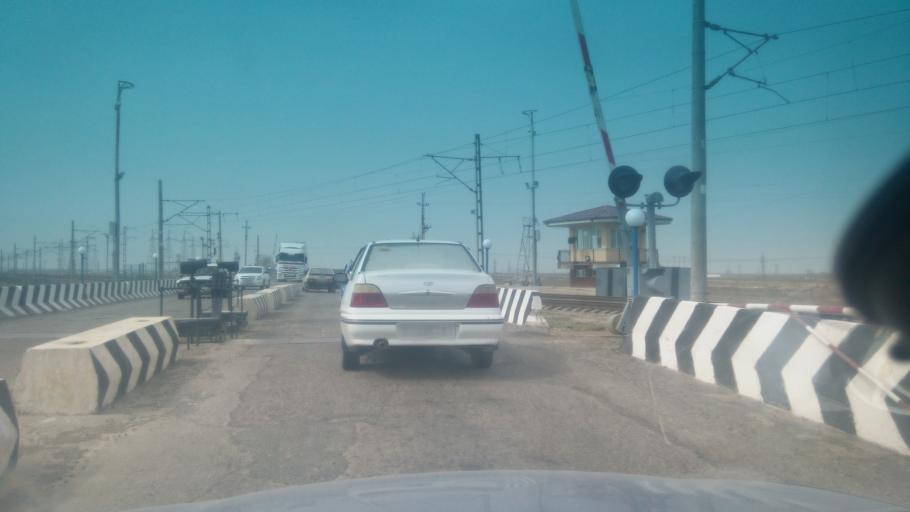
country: UZ
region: Jizzax
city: Dashtobod
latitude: 40.1495
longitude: 68.5320
